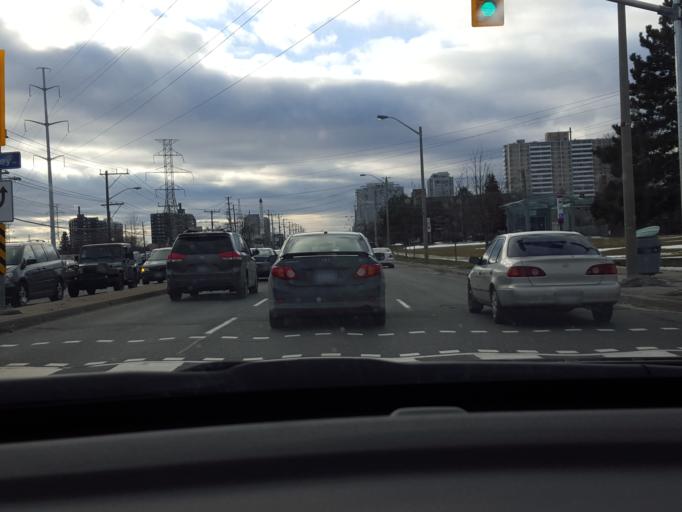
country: CA
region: Ontario
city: Scarborough
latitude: 43.7535
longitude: -79.2555
